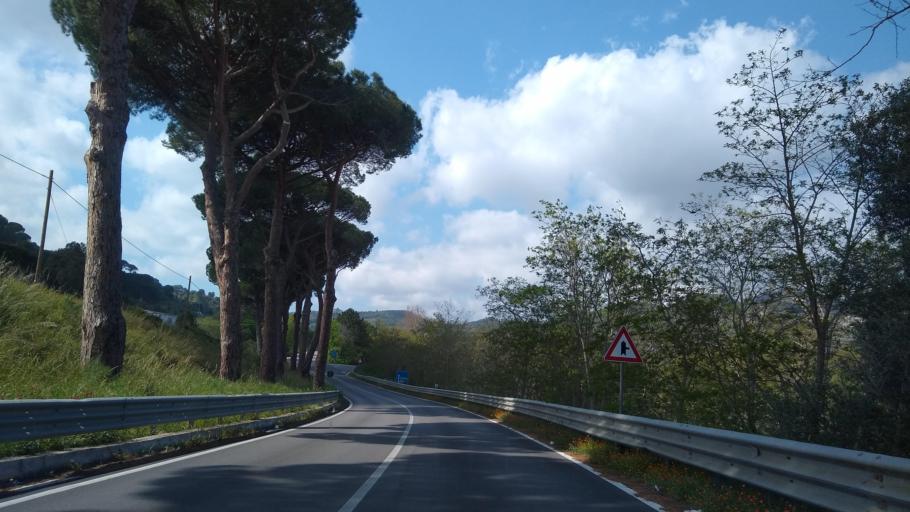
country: IT
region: Sicily
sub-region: Trapani
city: Calatafimi
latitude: 37.9370
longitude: 12.8542
